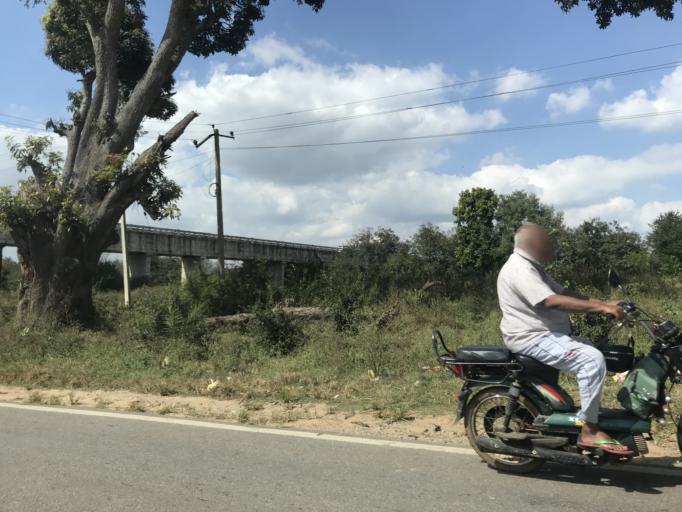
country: IN
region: Karnataka
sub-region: Hassan
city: Hassan
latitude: 12.9929
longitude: 76.0631
